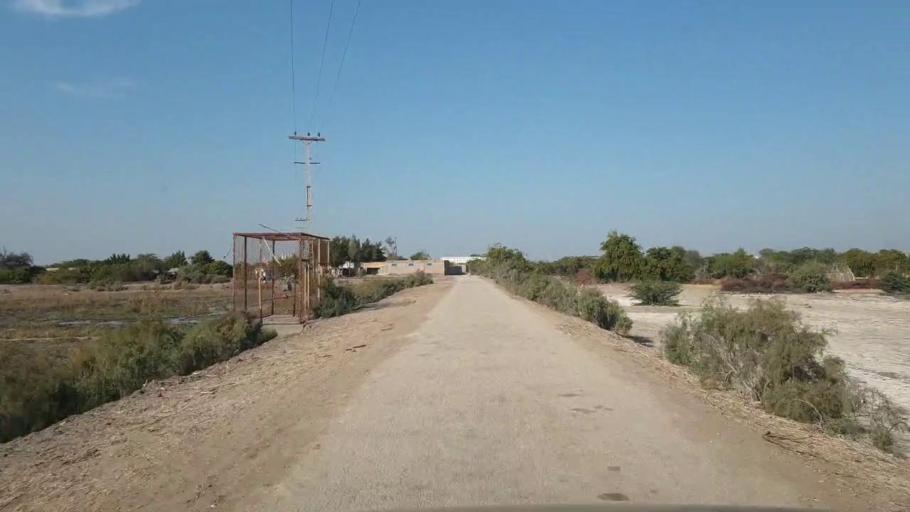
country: PK
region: Sindh
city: Shahpur Chakar
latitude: 26.1545
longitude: 68.6839
